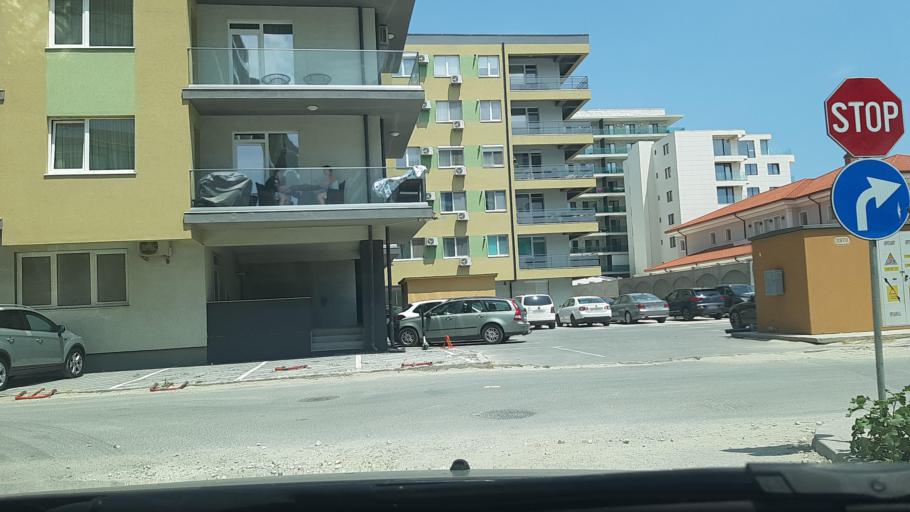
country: RO
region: Constanta
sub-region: Comuna Navodari
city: Navodari
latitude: 44.2878
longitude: 28.6219
